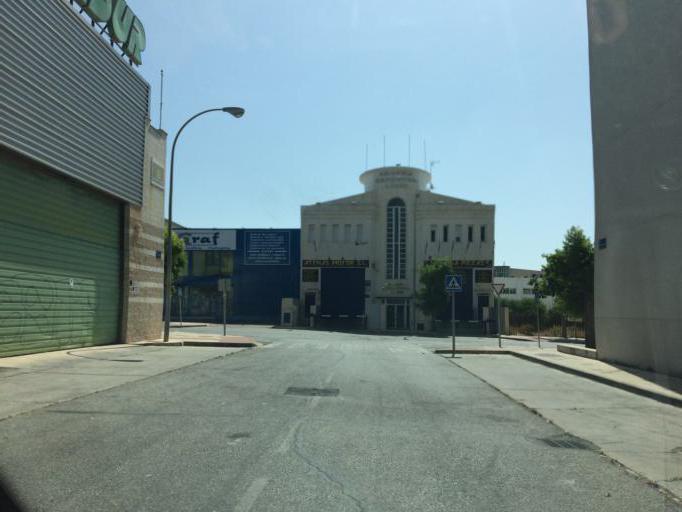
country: ES
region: Andalusia
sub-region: Provincia de Malaga
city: Malaga
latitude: 36.7075
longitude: -4.4698
